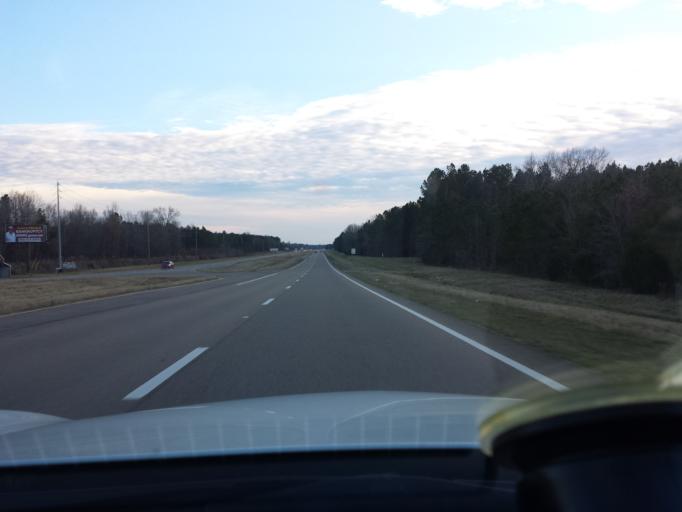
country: US
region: Mississippi
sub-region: Oktibbeha County
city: Starkville
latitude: 33.4369
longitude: -88.8540
